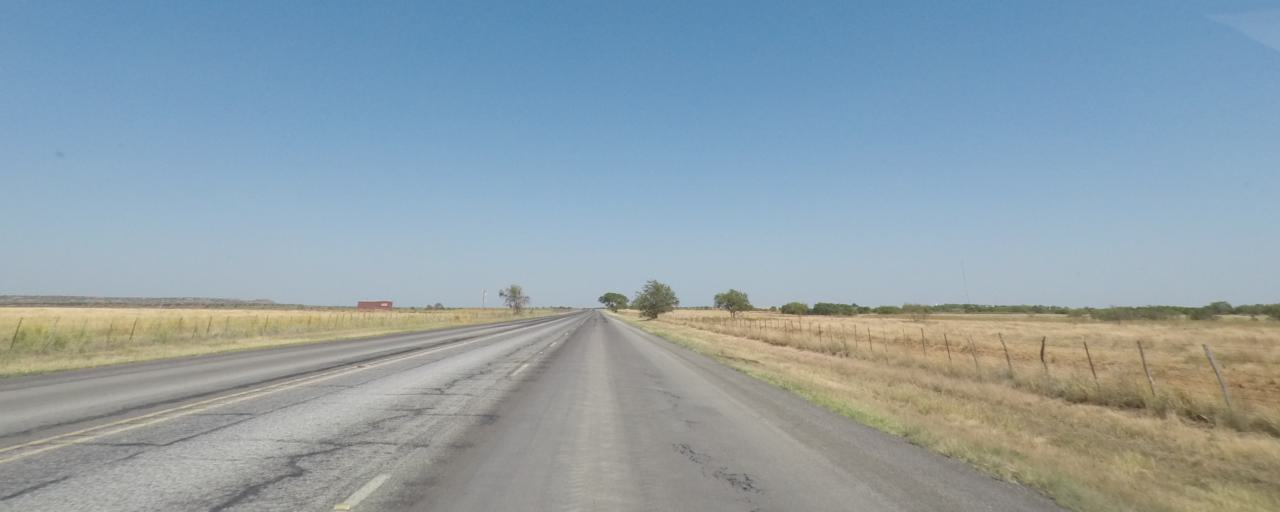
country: US
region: Texas
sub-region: King County
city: Guthrie
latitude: 33.6326
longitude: -100.3545
